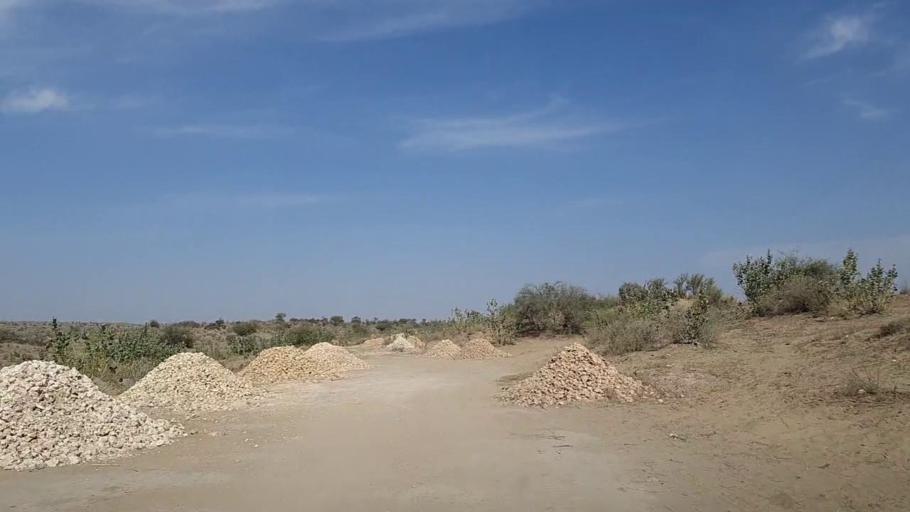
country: PK
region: Sindh
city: Umarkot
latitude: 25.2531
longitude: 69.9092
